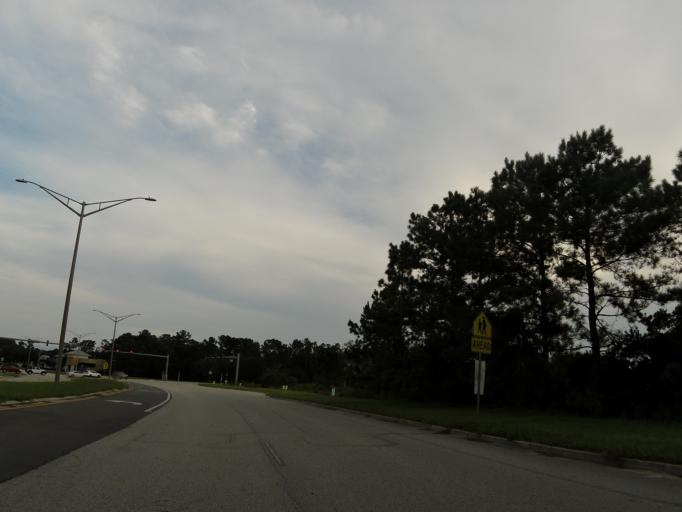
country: US
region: Florida
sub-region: Saint Johns County
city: Ponte Vedra Beach
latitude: 30.2376
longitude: -81.5198
